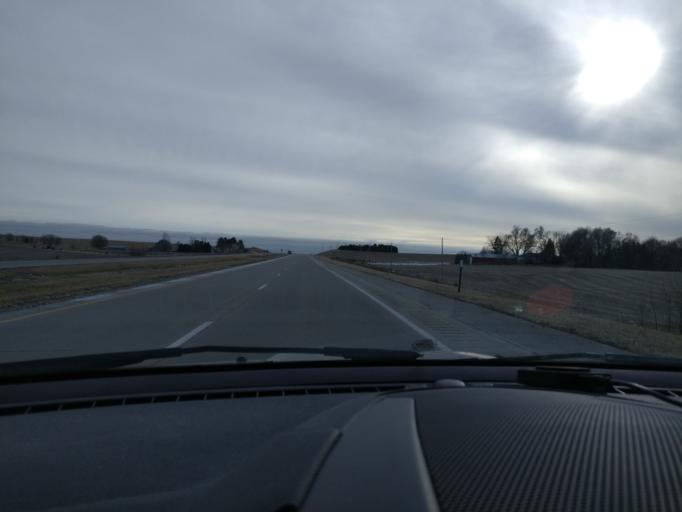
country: US
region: Nebraska
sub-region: Saunders County
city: Wahoo
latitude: 41.0922
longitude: -96.6401
